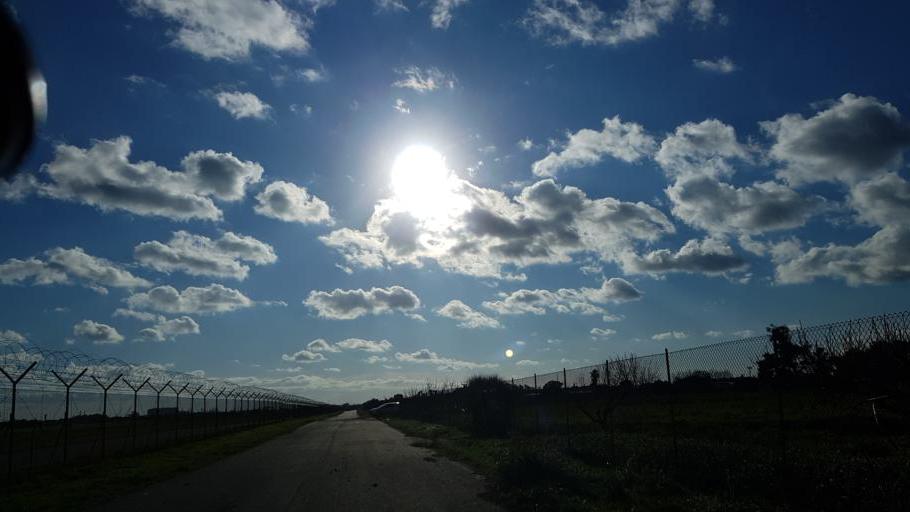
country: IT
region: Apulia
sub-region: Provincia di Brindisi
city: Materdomini
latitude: 40.6669
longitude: 17.9336
